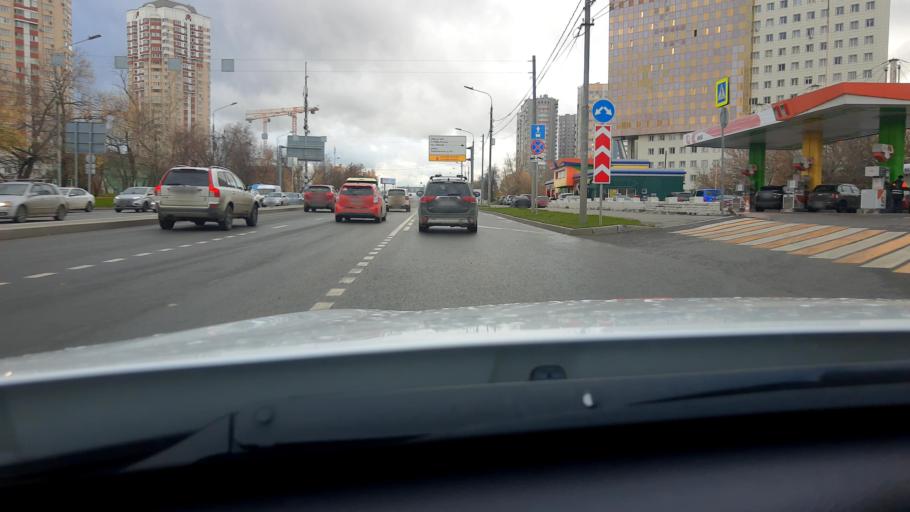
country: RU
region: Moscow
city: Nikol'skoye
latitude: 55.6884
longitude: 37.4747
